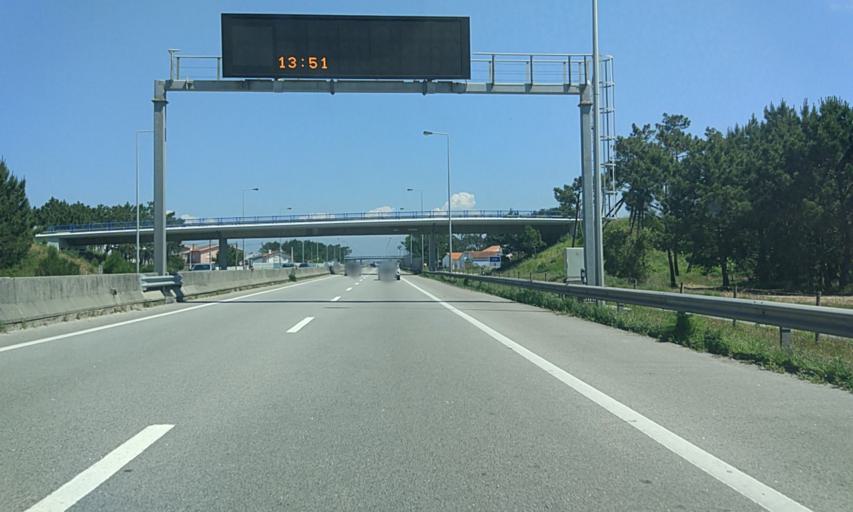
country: PT
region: Aveiro
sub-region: Ilhavo
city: Gafanha da Nazare
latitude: 40.6267
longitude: -8.7167
